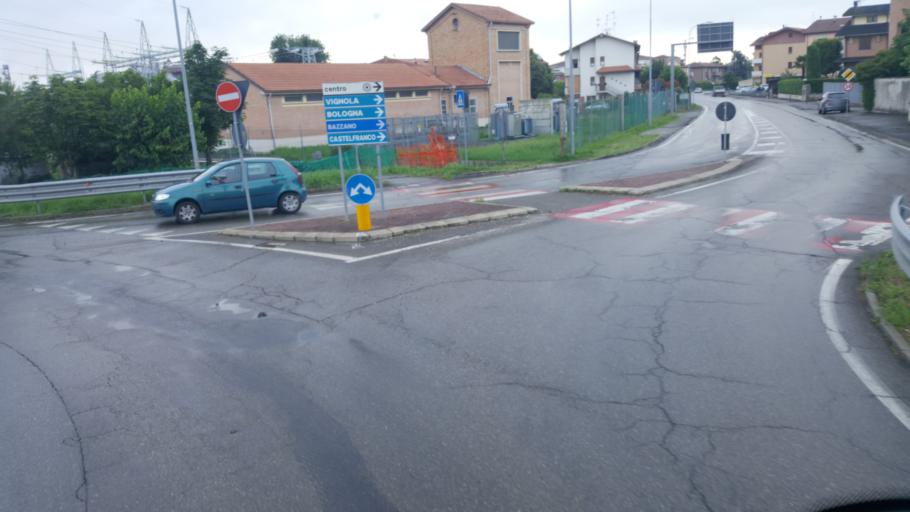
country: IT
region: Emilia-Romagna
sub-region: Provincia di Modena
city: Spilamberto
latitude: 44.5352
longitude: 11.0144
